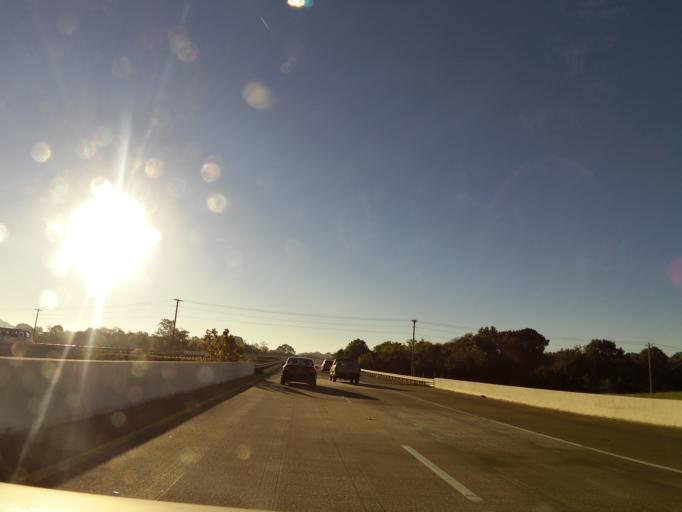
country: US
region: Tennessee
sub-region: Blount County
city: Alcoa
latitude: 35.8277
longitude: -83.9594
